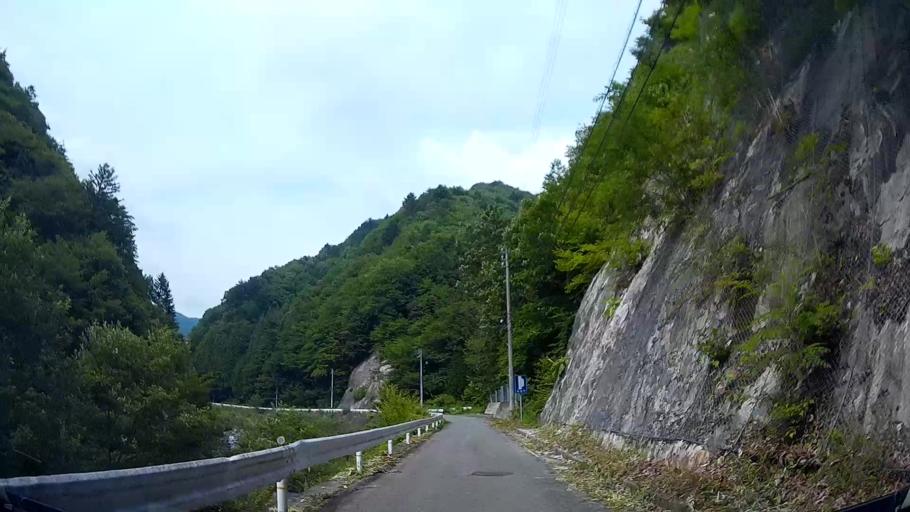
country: JP
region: Nagano
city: Iida
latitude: 35.4540
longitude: 137.9973
